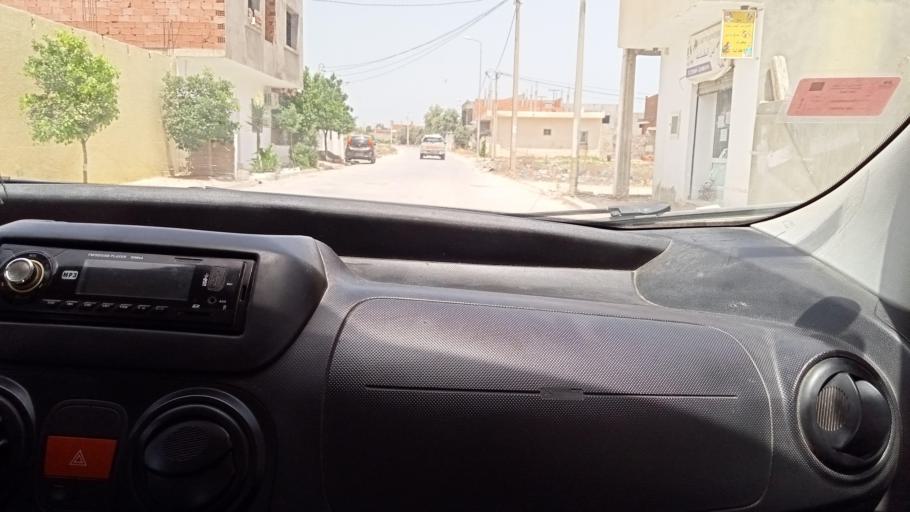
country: TN
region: Nabul
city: Qulaybiyah
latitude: 36.8610
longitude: 11.0873
